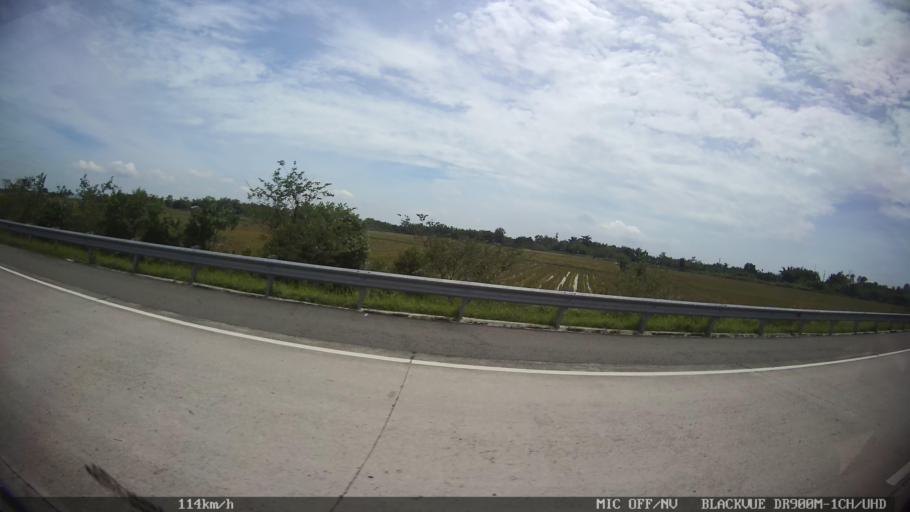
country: ID
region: North Sumatra
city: Percut
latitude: 3.5664
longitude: 98.8490
